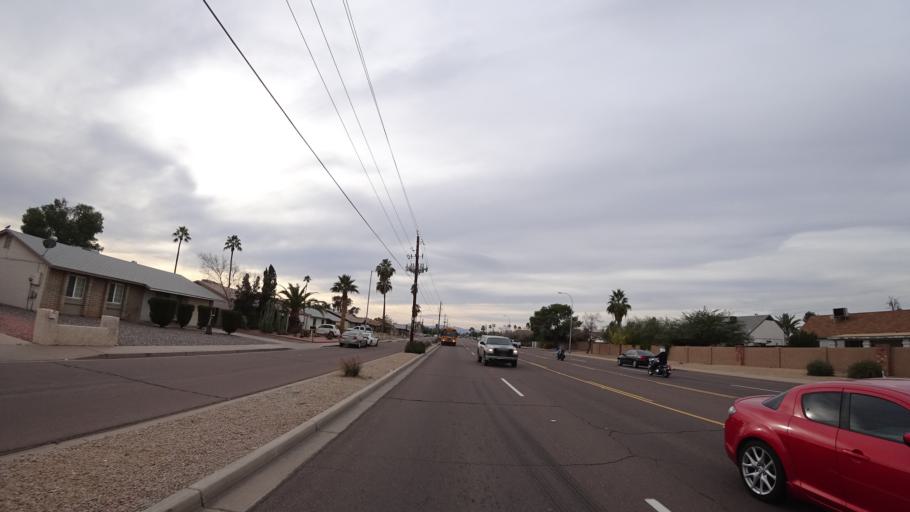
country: US
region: Arizona
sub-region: Maricopa County
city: Peoria
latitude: 33.5814
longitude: -112.2137
